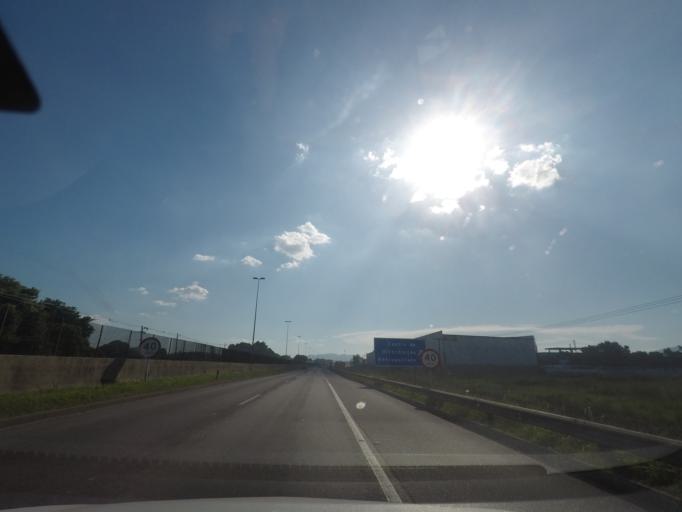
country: BR
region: Rio de Janeiro
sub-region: Duque De Caxias
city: Duque de Caxias
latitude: -22.6630
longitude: -43.2568
